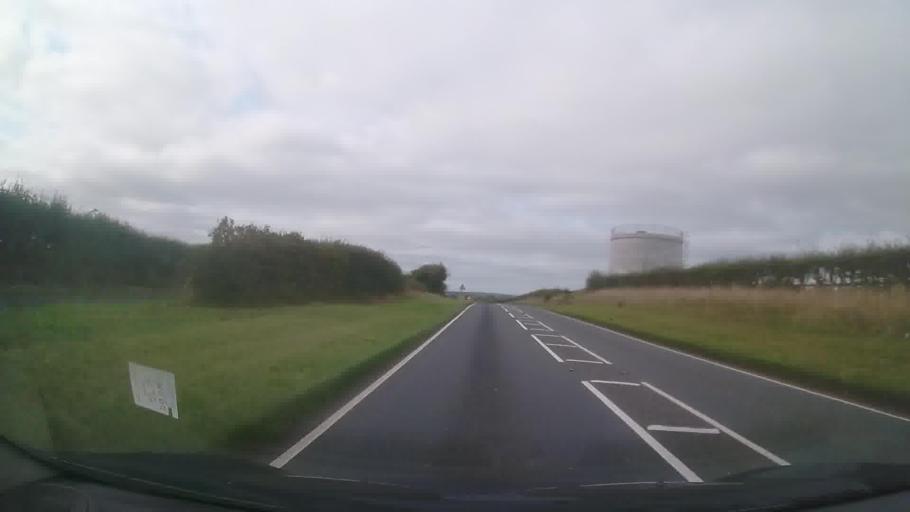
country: GB
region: Wales
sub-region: Pembrokeshire
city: Neyland
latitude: 51.7233
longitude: -4.9696
